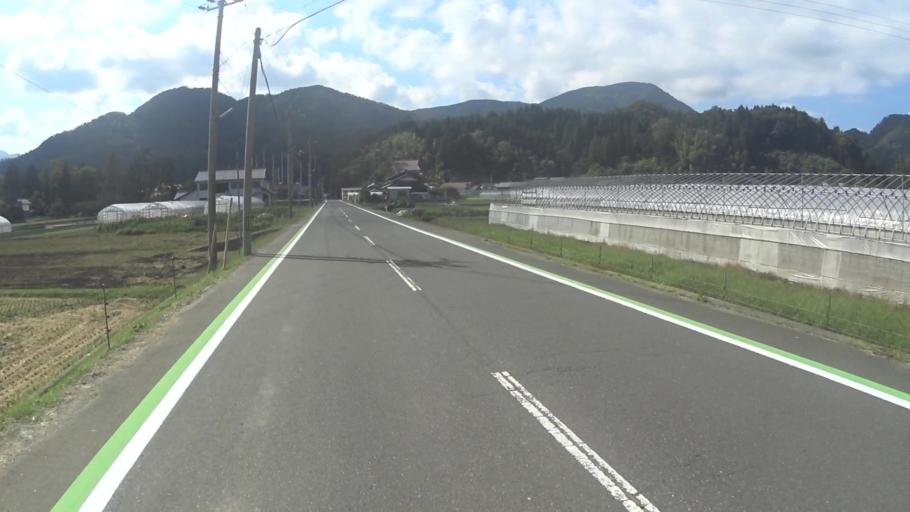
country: JP
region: Kyoto
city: Miyazu
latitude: 35.7299
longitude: 135.2600
